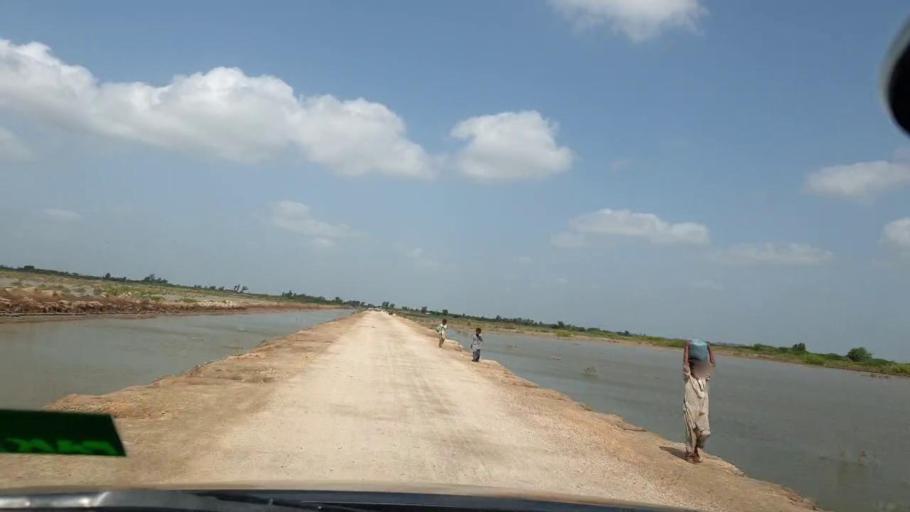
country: PK
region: Sindh
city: Kadhan
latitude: 24.5968
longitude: 69.1288
